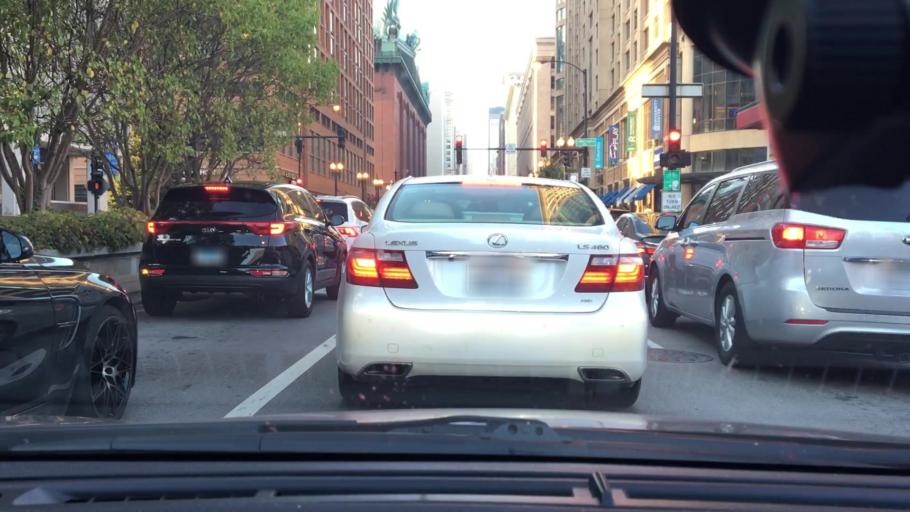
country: US
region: Illinois
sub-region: Cook County
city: Chicago
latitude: 41.8740
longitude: -87.6276
